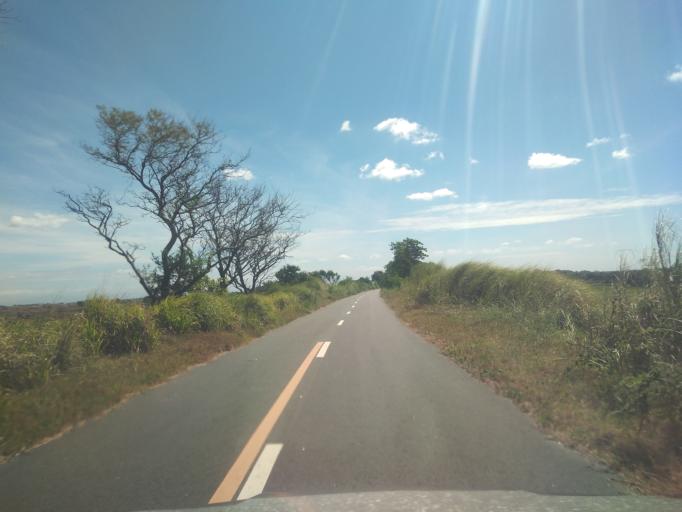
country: PH
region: Central Luzon
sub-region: Province of Pampanga
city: Balas
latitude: 15.0473
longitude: 120.5910
